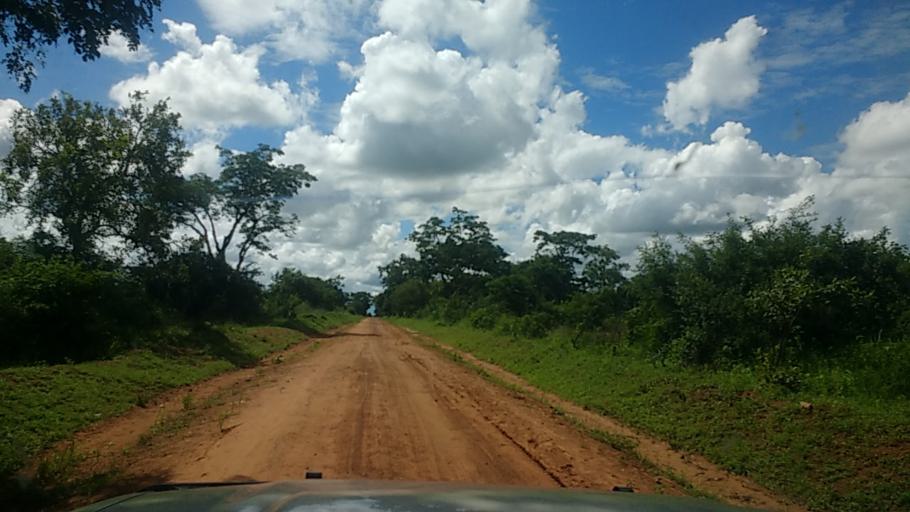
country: UG
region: Eastern Region
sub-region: Katakwi District
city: Katakwi
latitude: 1.7657
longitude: 33.9534
